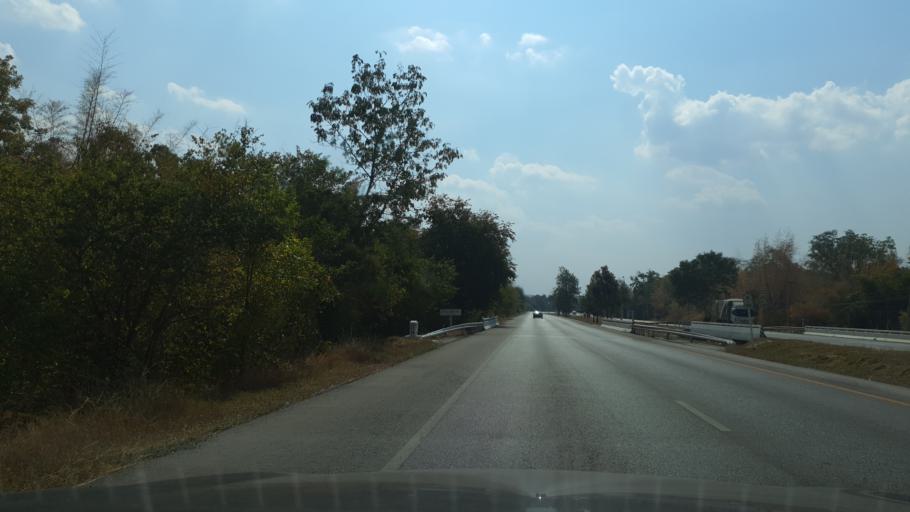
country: TH
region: Lampang
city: Mae Phrik
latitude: 17.4243
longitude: 99.1578
